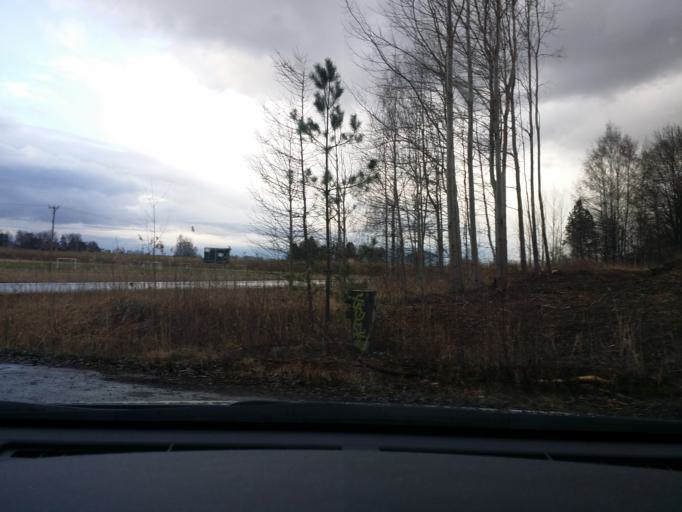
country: SE
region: Soedermanland
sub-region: Eskilstuna Kommun
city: Arla
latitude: 59.3838
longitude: 16.6835
